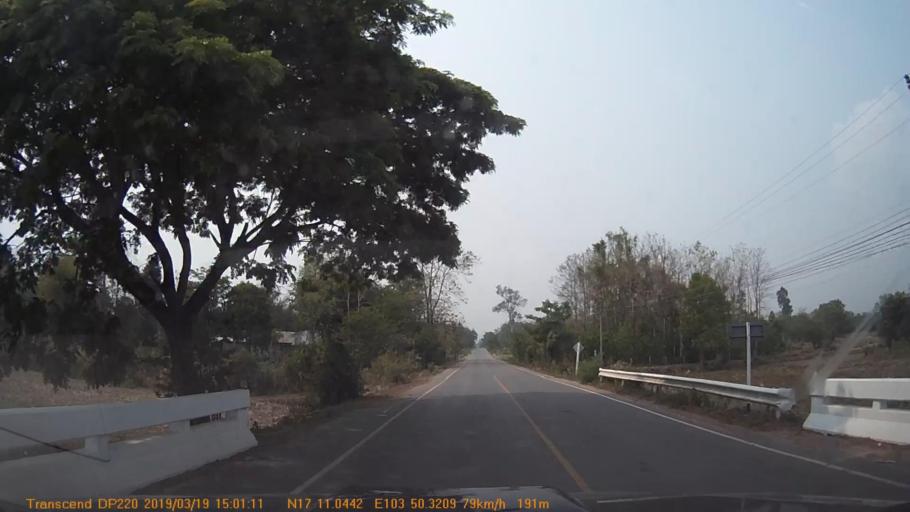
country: TH
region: Sakon Nakhon
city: Kut Bak
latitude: 17.1844
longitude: 103.8385
